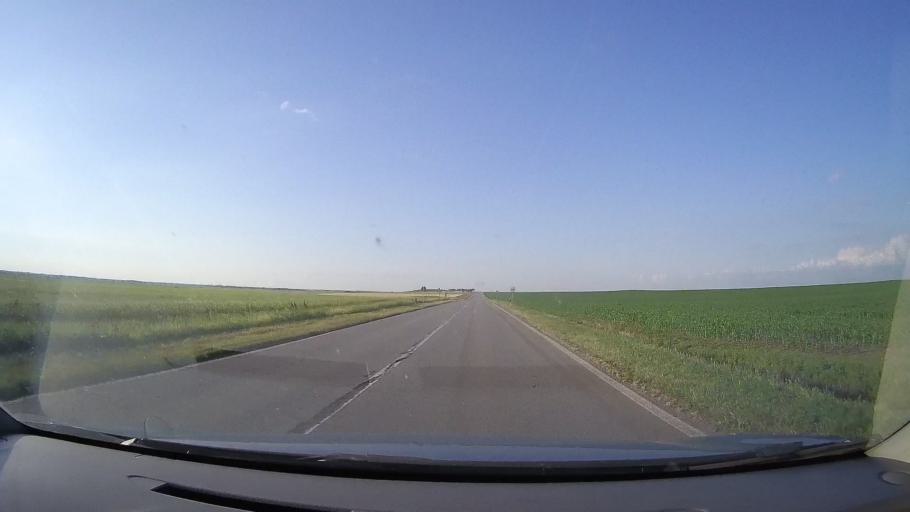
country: RS
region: Autonomna Pokrajina Vojvodina
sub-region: Juznobanatski Okrug
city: Vrsac
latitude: 45.1880
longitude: 21.2978
